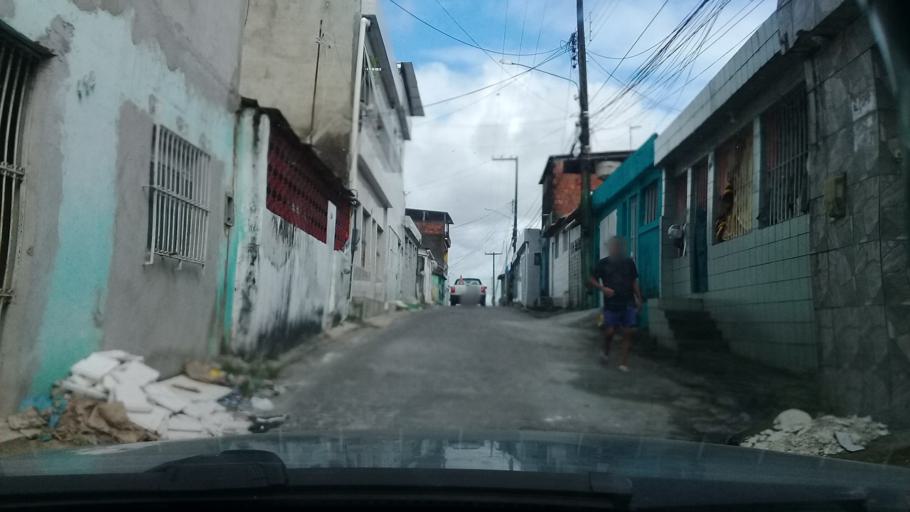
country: BR
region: Pernambuco
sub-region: Jaboatao Dos Guararapes
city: Jaboatao dos Guararapes
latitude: -8.1127
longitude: -34.9646
